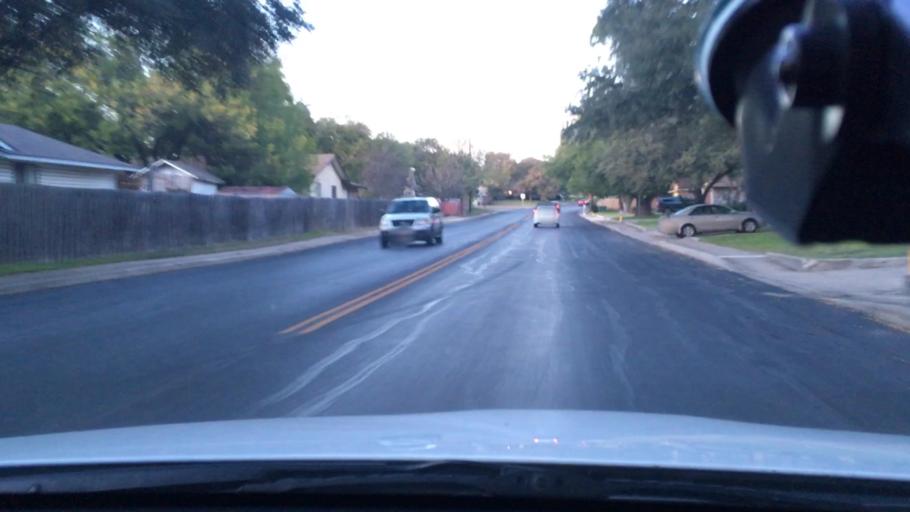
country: US
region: Texas
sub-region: Bexar County
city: Windcrest
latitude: 29.5149
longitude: -98.3566
